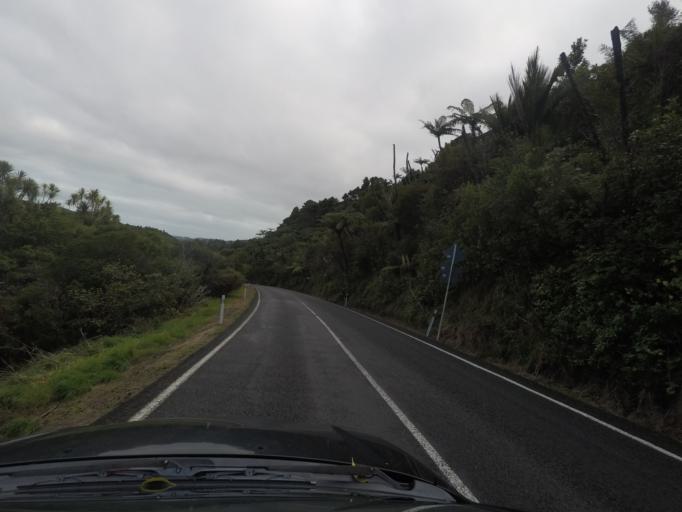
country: NZ
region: Auckland
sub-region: Auckland
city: Muriwai Beach
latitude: -36.8763
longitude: 174.5316
